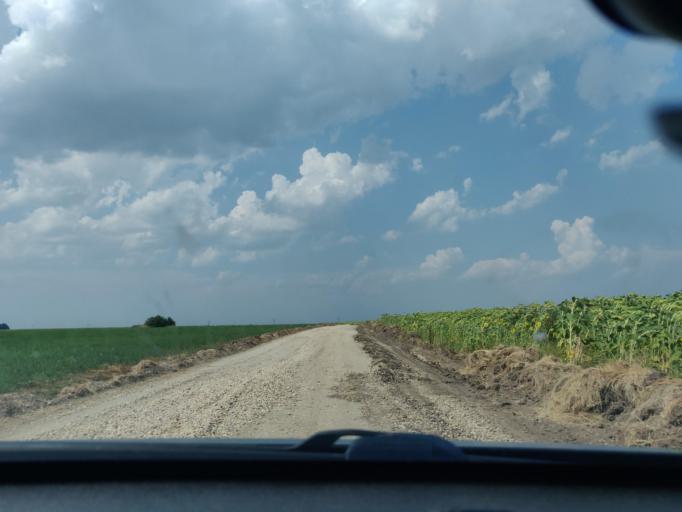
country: RO
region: Teleorman
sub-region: Comuna Sarbeni
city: Sarbeni
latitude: 44.5012
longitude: 25.3977
